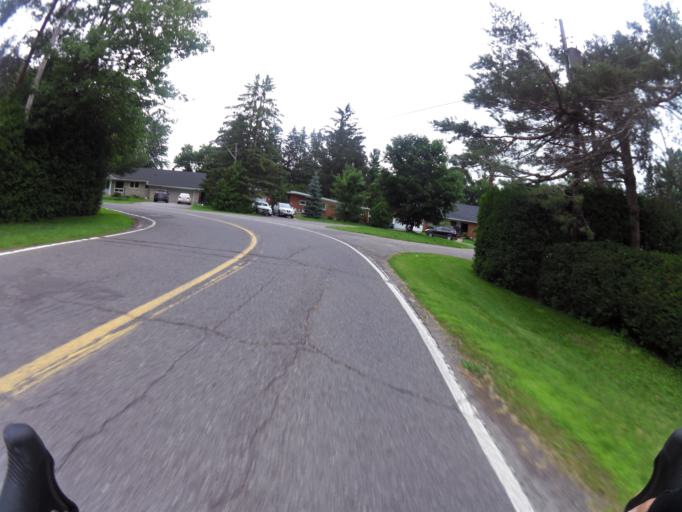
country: CA
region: Ontario
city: Ottawa
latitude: 45.3284
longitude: -75.7035
